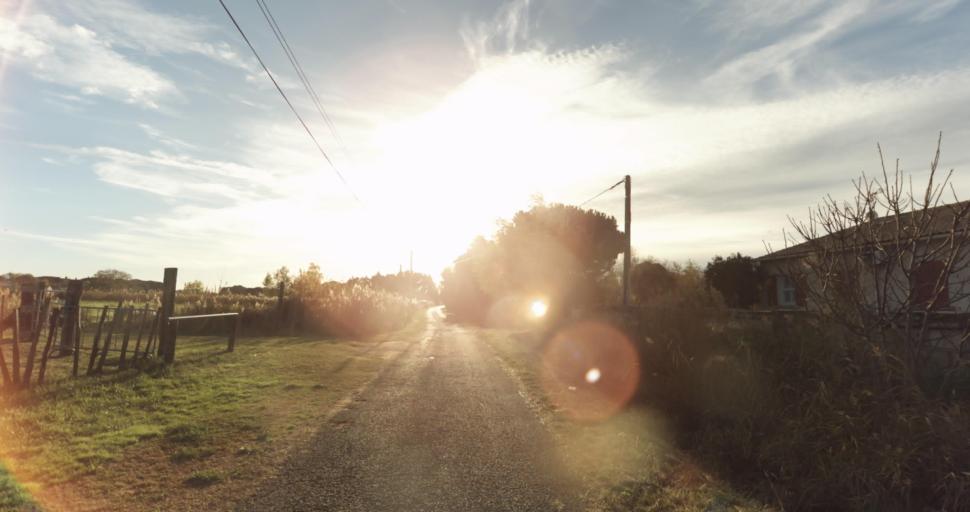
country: FR
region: Languedoc-Roussillon
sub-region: Departement du Gard
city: Aigues-Mortes
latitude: 43.5609
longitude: 4.1997
